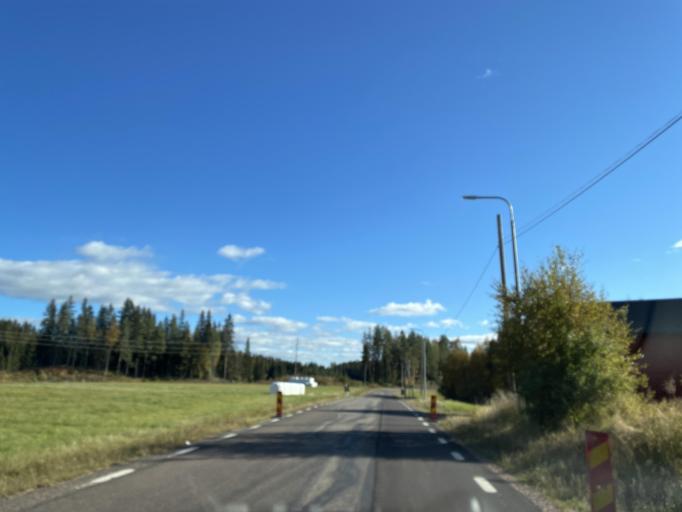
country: SE
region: Dalarna
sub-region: Malung-Saelens kommun
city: Malung
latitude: 60.8675
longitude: 13.4013
